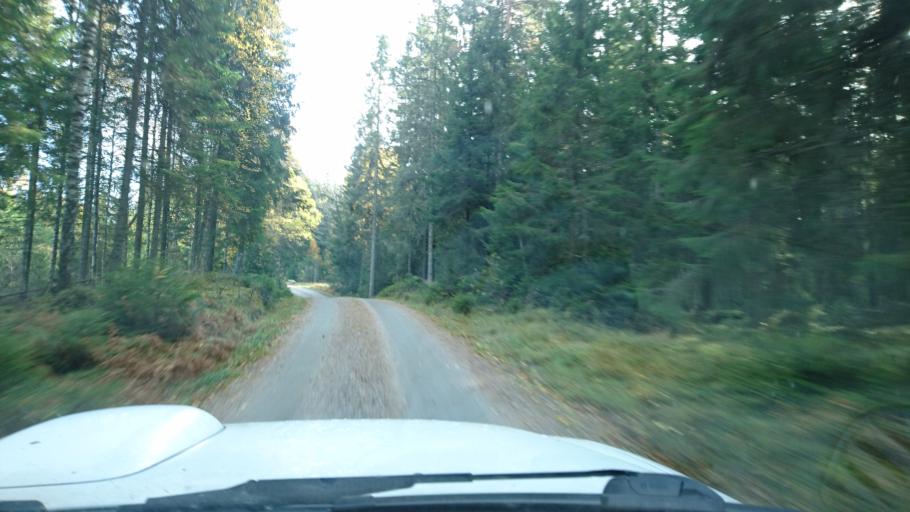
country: SE
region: Vaestra Goetaland
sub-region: Ulricehamns Kommun
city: Ulricehamn
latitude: 57.9431
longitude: 13.5440
